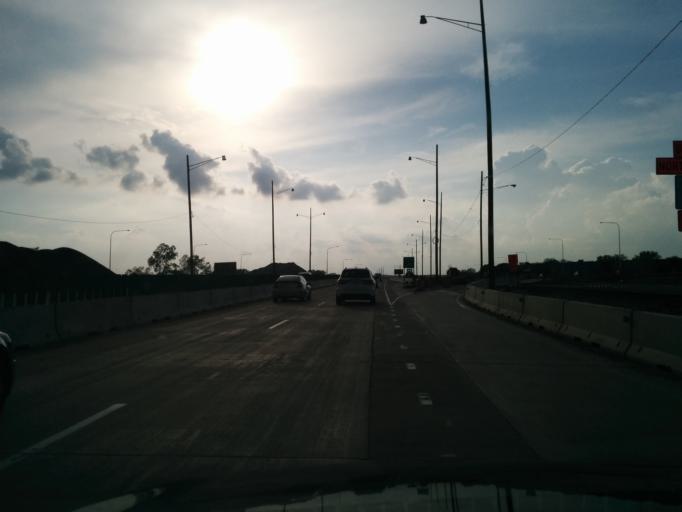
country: US
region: Illinois
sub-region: DuPage County
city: Itasca
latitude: 41.9886
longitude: -88.0352
